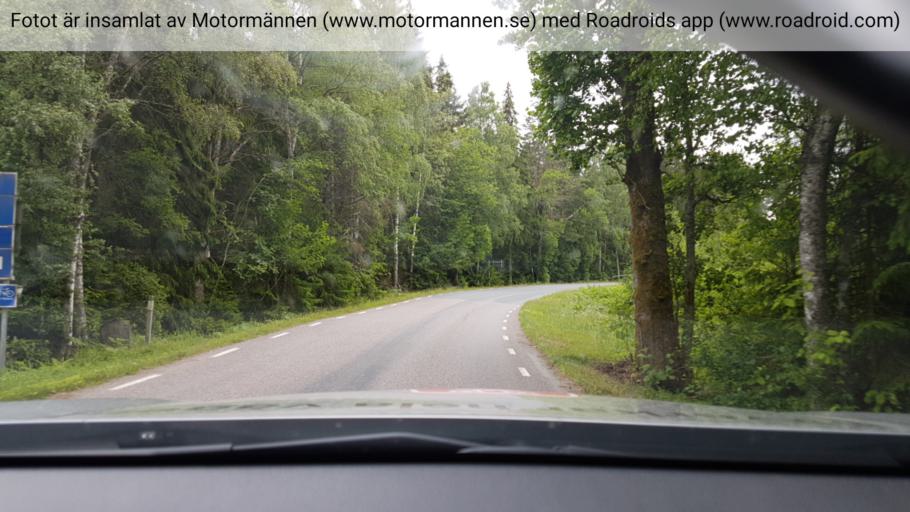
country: SE
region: Joenkoeping
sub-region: Habo Kommun
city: Habo
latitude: 58.0134
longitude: 14.0062
